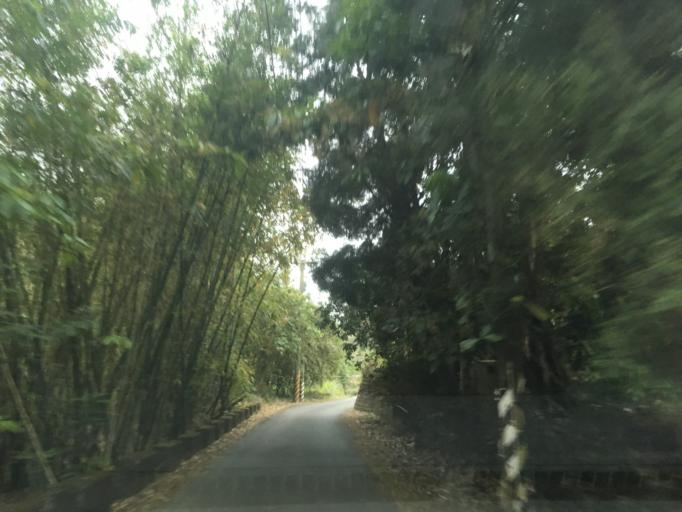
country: TW
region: Taiwan
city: Zhongxing New Village
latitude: 24.0378
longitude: 120.7581
